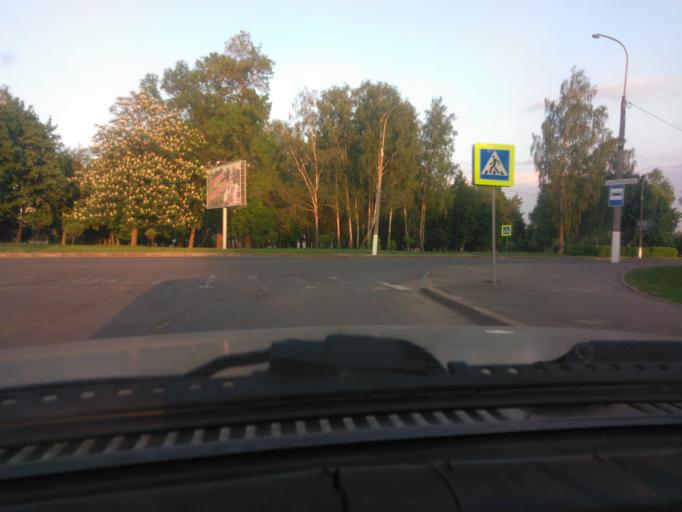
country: BY
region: Mogilev
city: Mahilyow
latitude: 53.9278
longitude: 30.3124
